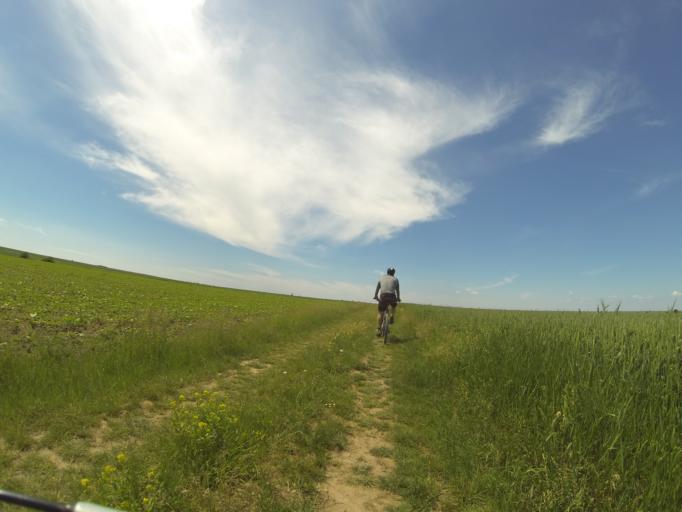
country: RO
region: Dolj
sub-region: Comuna Teslui
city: Teslui
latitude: 44.1941
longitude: 24.1399
